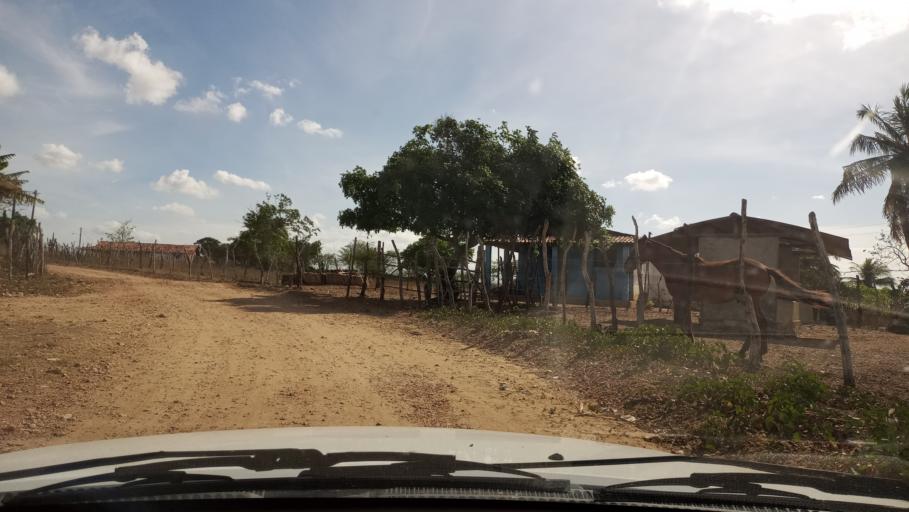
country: BR
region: Rio Grande do Norte
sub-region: Goianinha
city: Goianinha
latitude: -6.3097
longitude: -35.3068
